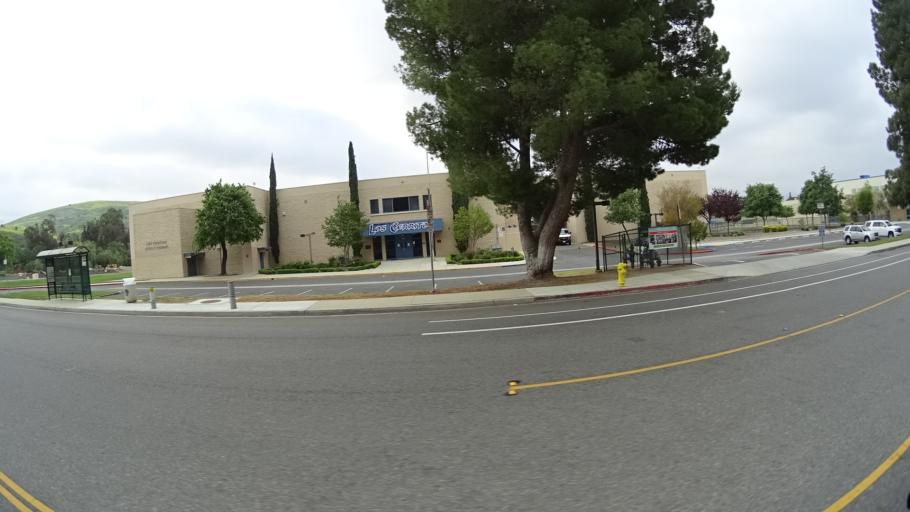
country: US
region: California
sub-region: Ventura County
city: Thousand Oaks
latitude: 34.2079
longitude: -118.8404
